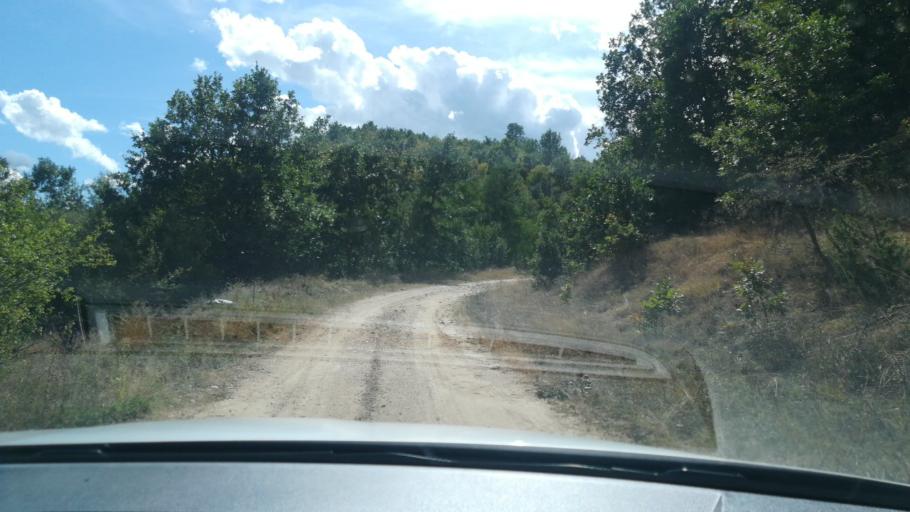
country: MK
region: Delcevo
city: Delcevo
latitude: 41.8975
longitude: 22.8053
